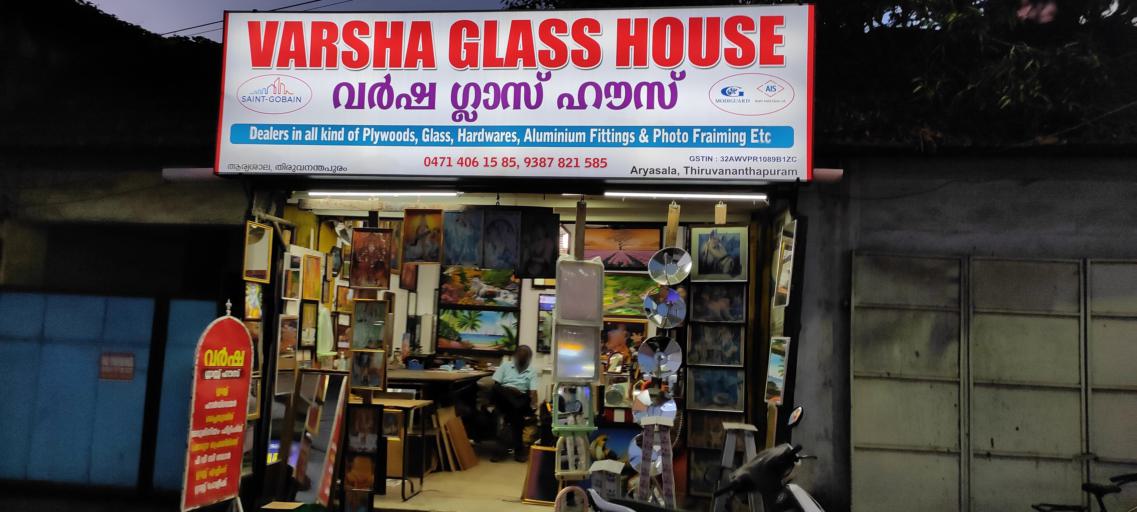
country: IN
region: Kerala
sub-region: Thiruvananthapuram
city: Thiruvananthapuram
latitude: 8.4818
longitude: 76.9550
